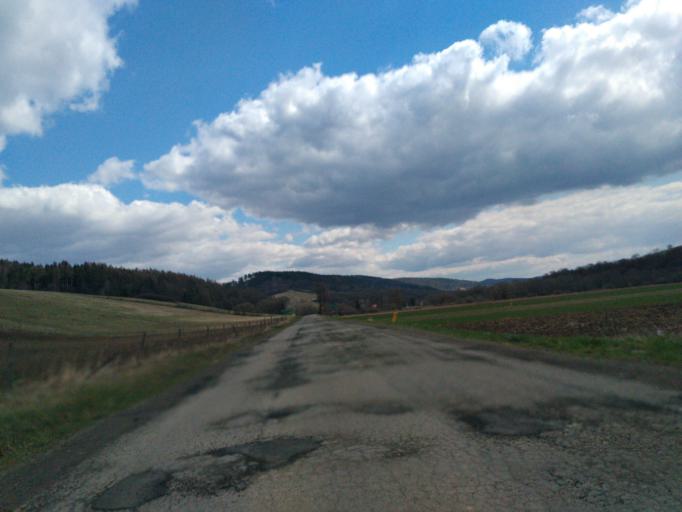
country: PL
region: Subcarpathian Voivodeship
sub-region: Powiat sanocki
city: Tyrawa Woloska
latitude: 49.6056
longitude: 22.2992
